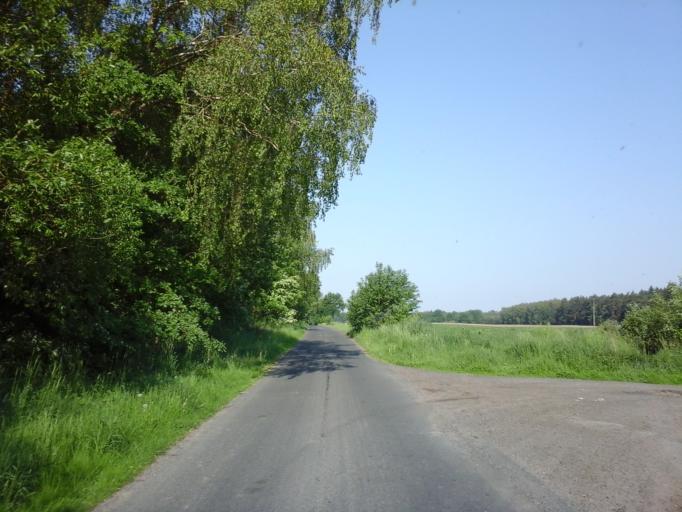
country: PL
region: West Pomeranian Voivodeship
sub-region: Powiat choszczenski
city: Recz
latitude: 53.2915
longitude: 15.5381
